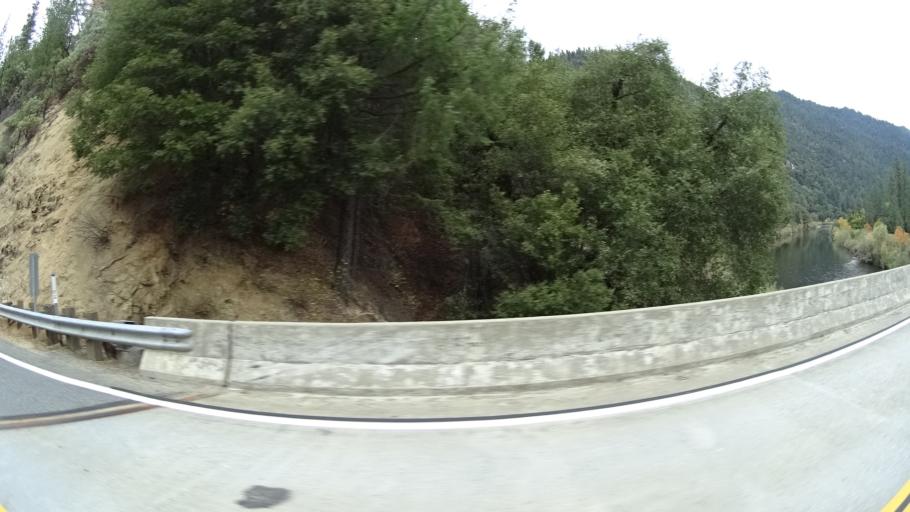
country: US
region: California
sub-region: Siskiyou County
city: Happy Camp
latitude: 41.8348
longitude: -123.1820
